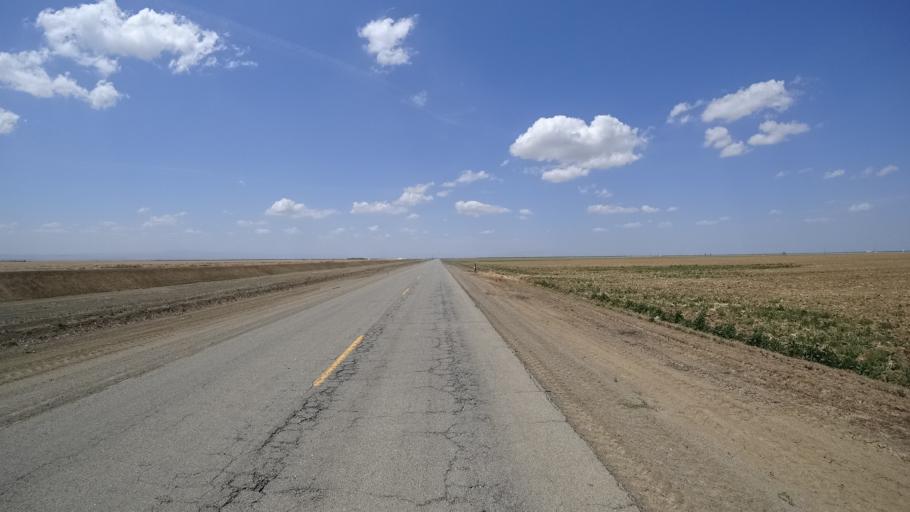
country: US
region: California
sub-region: Kings County
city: Lemoore Station
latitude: 36.1894
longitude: -119.9101
